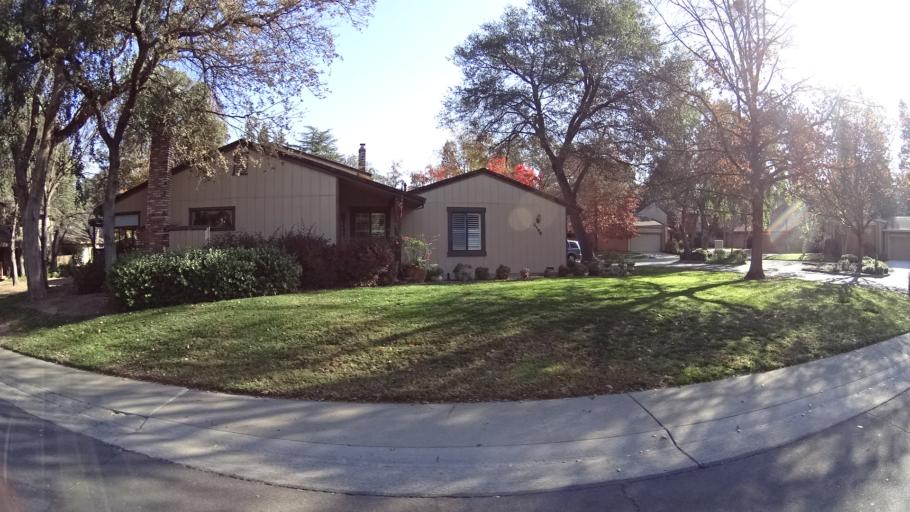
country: US
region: California
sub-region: Sacramento County
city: Citrus Heights
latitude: 38.6829
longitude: -121.3019
